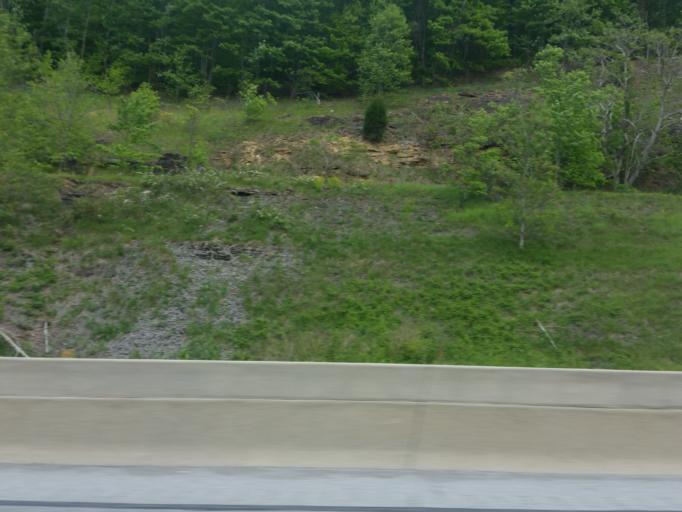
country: US
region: West Virginia
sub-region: Fayette County
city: Oak Hill
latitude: 37.9827
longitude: -81.3015
